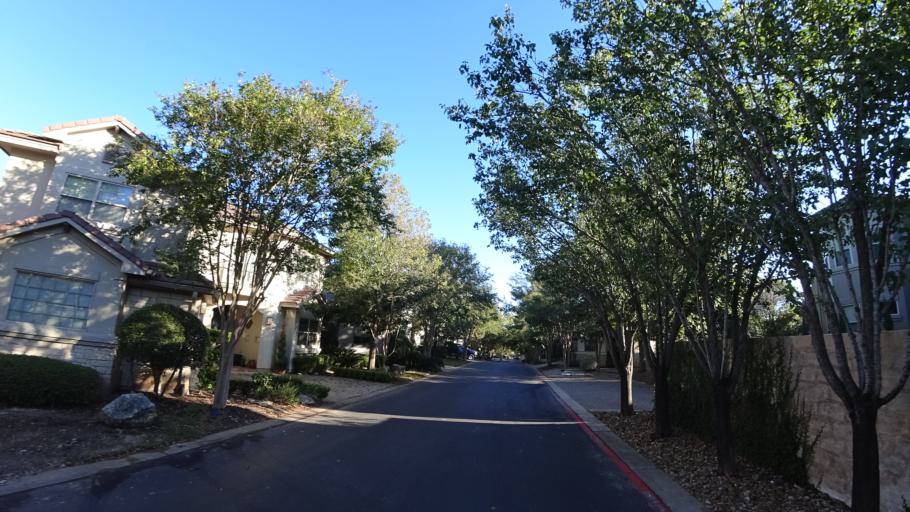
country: US
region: Texas
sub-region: Travis County
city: West Lake Hills
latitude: 30.3239
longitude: -97.8120
